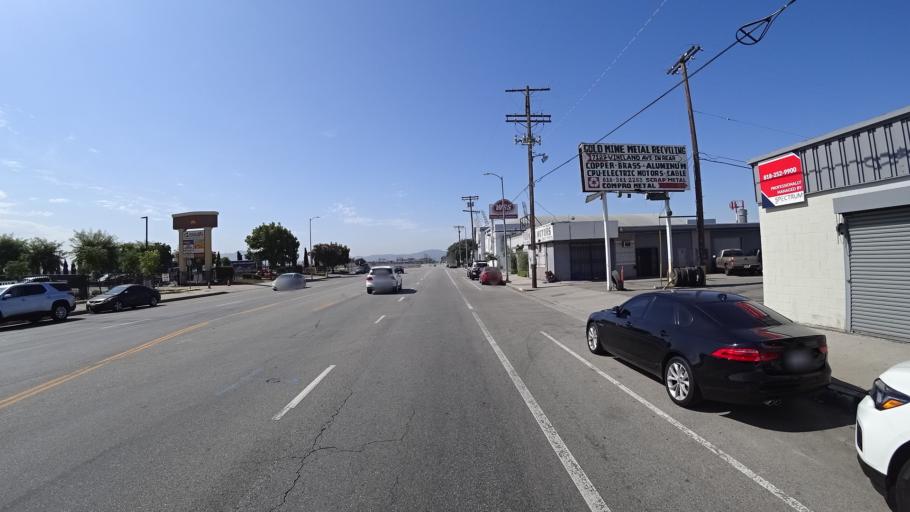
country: US
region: California
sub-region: Los Angeles County
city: North Hollywood
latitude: 34.2005
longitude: -118.3704
